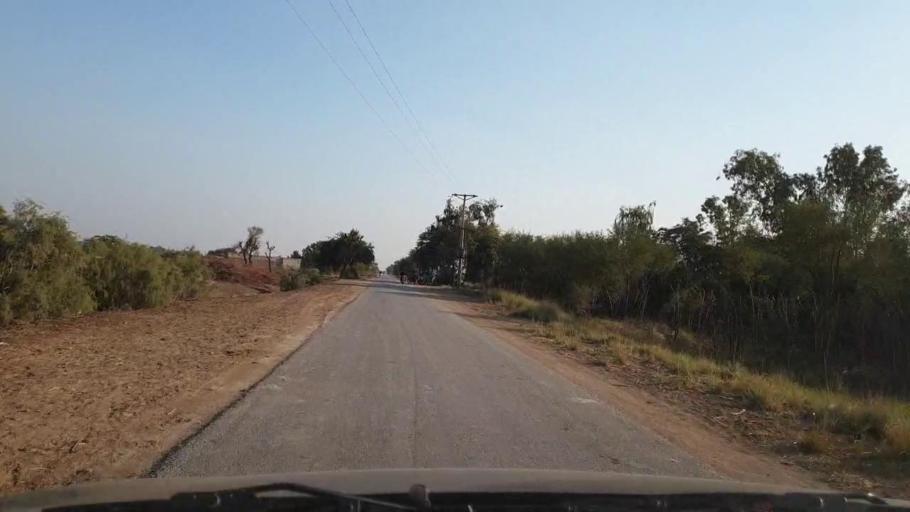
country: PK
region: Sindh
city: Jhol
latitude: 25.9541
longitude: 68.8992
